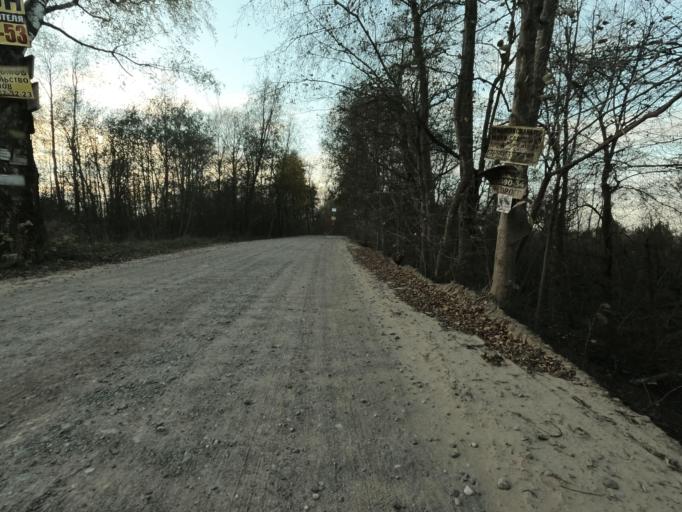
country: RU
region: Leningrad
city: Mga
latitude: 59.7702
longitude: 31.2295
